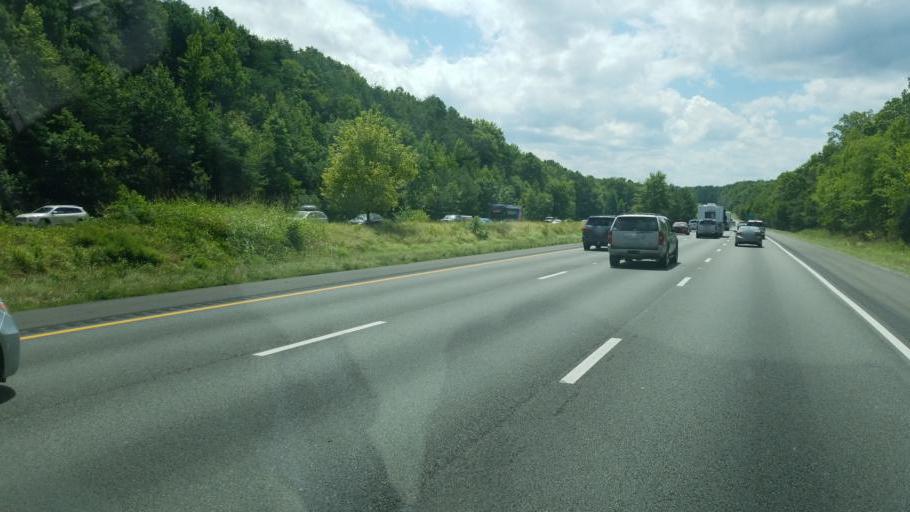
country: US
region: Virginia
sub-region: Hanover County
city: Ashland
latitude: 37.8151
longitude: -77.4596
